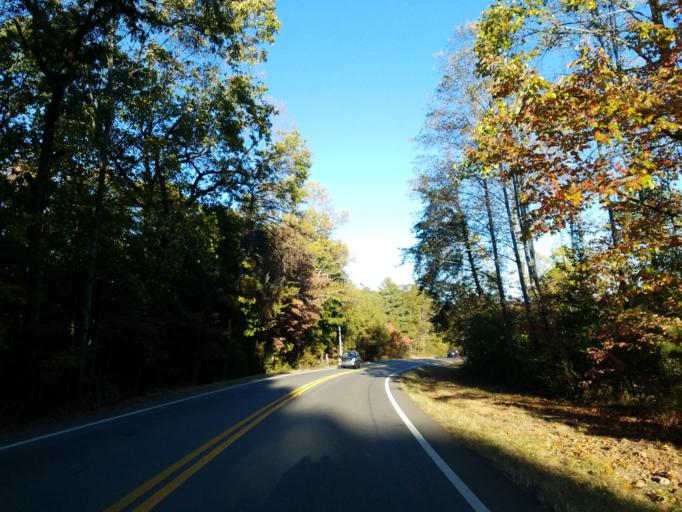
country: US
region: Georgia
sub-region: Dawson County
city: Dawsonville
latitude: 34.4260
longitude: -84.2319
